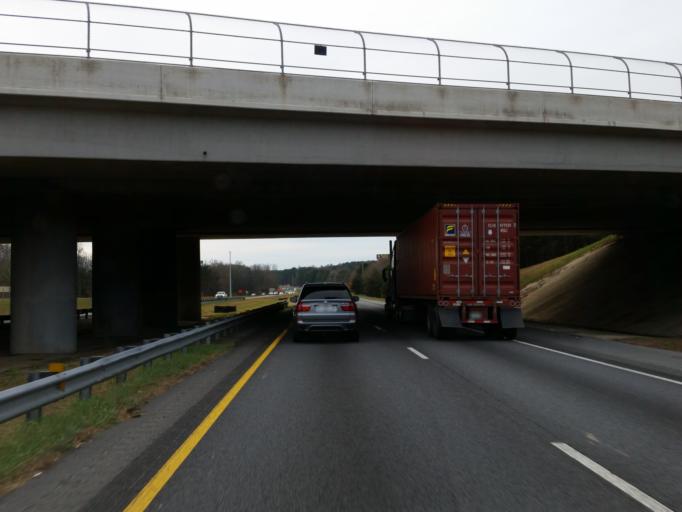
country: US
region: Georgia
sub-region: Cherokee County
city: Woodstock
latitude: 34.0859
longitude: -84.5355
